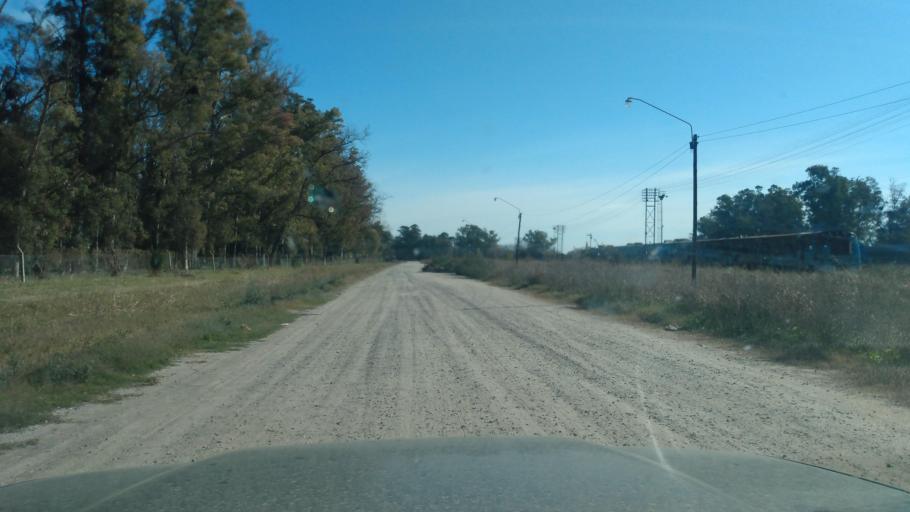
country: AR
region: Buenos Aires
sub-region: Partido de Lujan
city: Lujan
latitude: -34.5770
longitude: -59.0906
